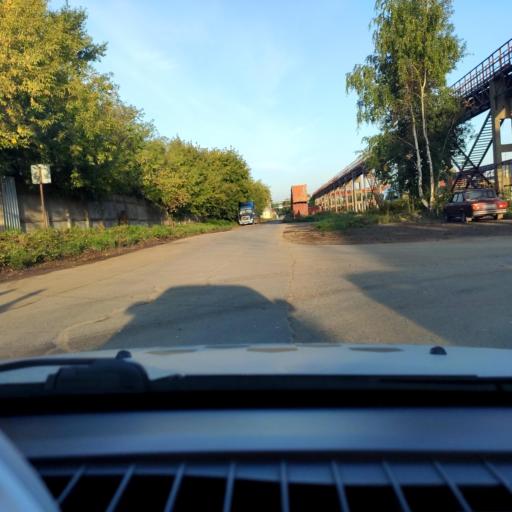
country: RU
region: Perm
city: Froly
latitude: 57.9545
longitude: 56.2585
